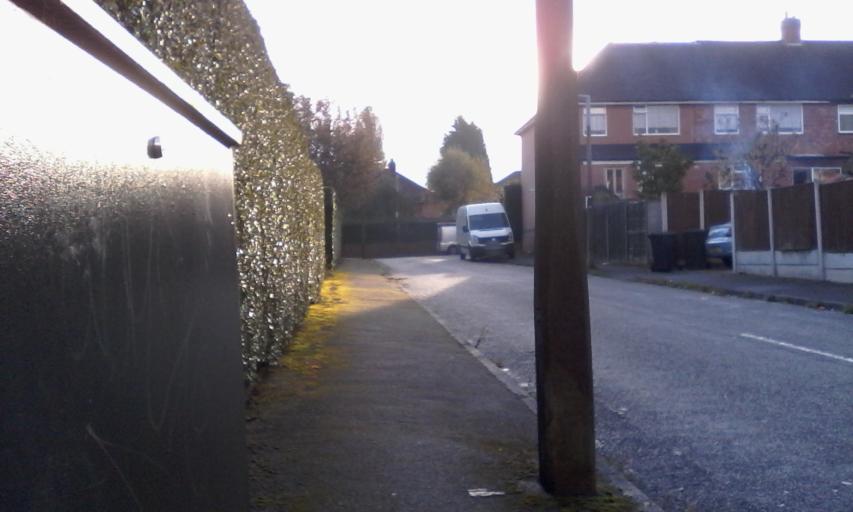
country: GB
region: England
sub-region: Nottinghamshire
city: Arnold
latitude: 52.9810
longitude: -1.1024
